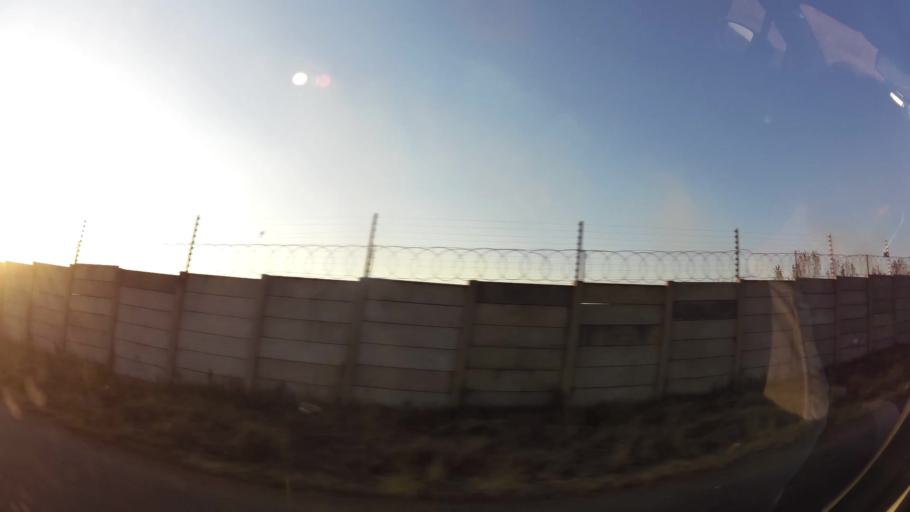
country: ZA
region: Gauteng
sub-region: West Rand District Municipality
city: Randfontein
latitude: -26.2022
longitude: 27.6833
